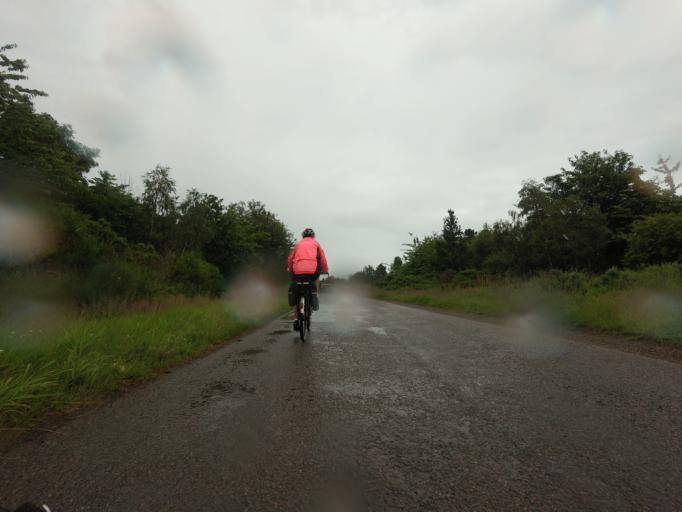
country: GB
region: Scotland
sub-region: Moray
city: Fochabers
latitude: 57.6596
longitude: -3.0677
